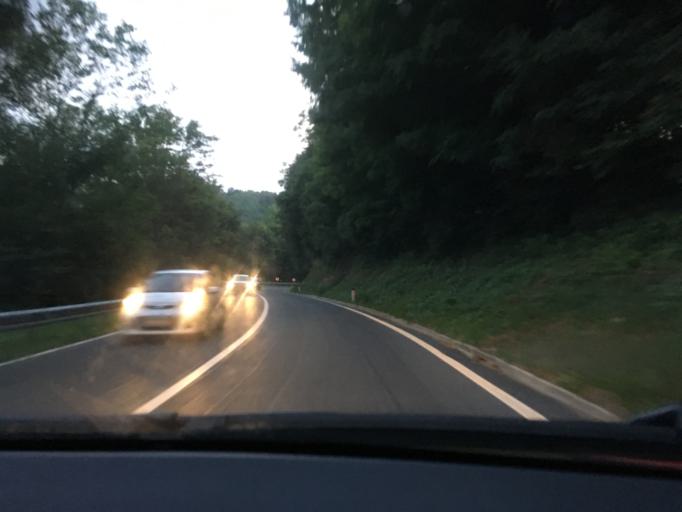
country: SI
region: Pivka
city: Pivka
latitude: 45.6013
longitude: 14.1977
